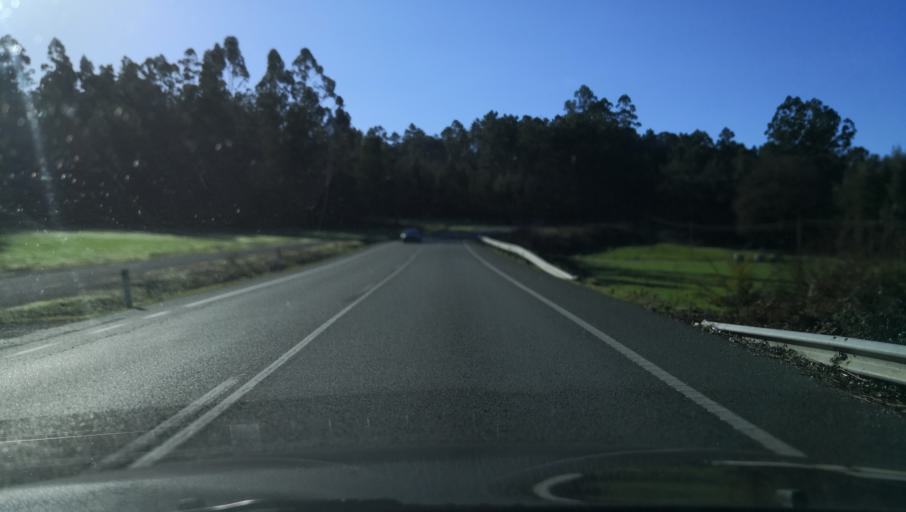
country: ES
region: Galicia
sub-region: Provincia da Coruna
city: Vedra
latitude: 42.8145
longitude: -8.4788
